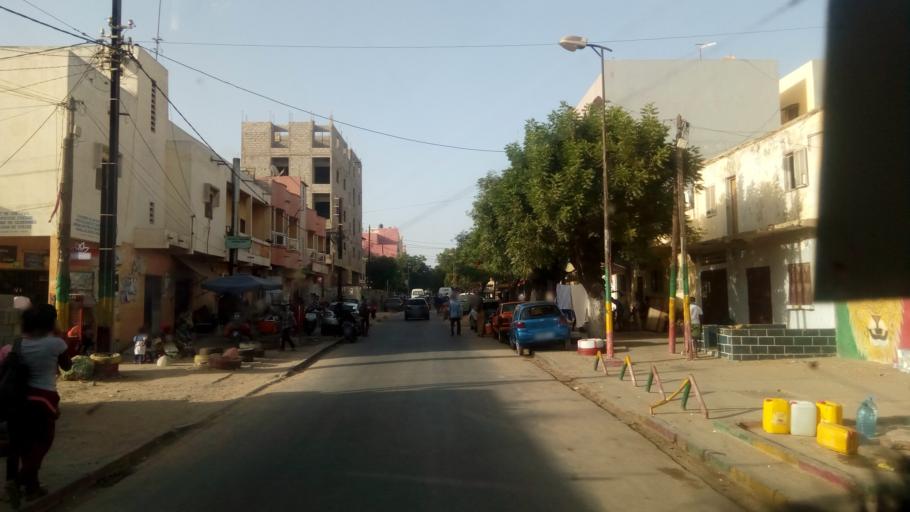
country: SN
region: Dakar
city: Grand Dakar
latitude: 14.7106
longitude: -17.4496
